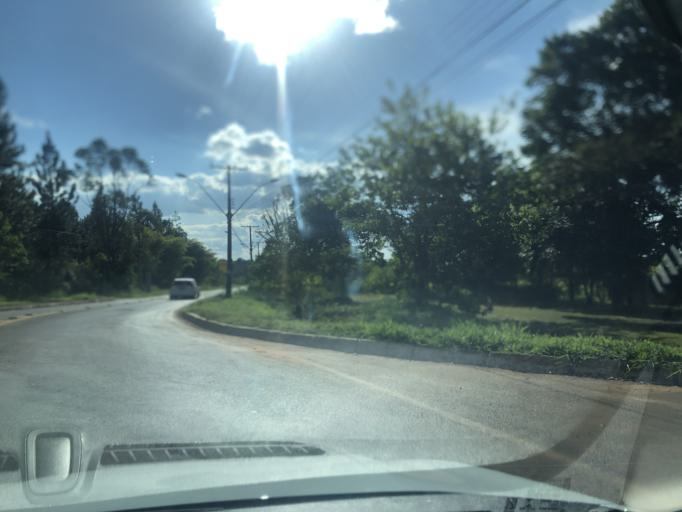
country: BR
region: Federal District
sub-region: Brasilia
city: Brasilia
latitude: -15.8967
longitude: -47.9380
